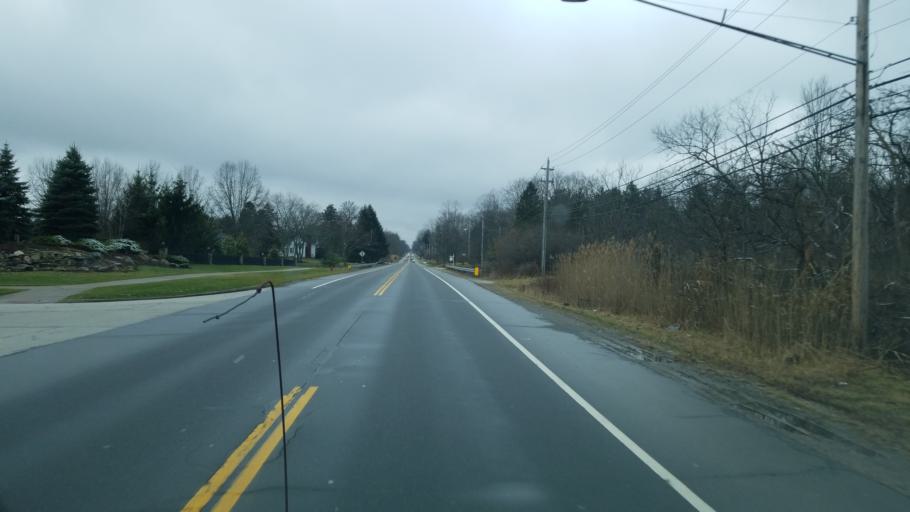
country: US
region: Ohio
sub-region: Summit County
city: Hudson
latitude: 41.2398
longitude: -81.3976
